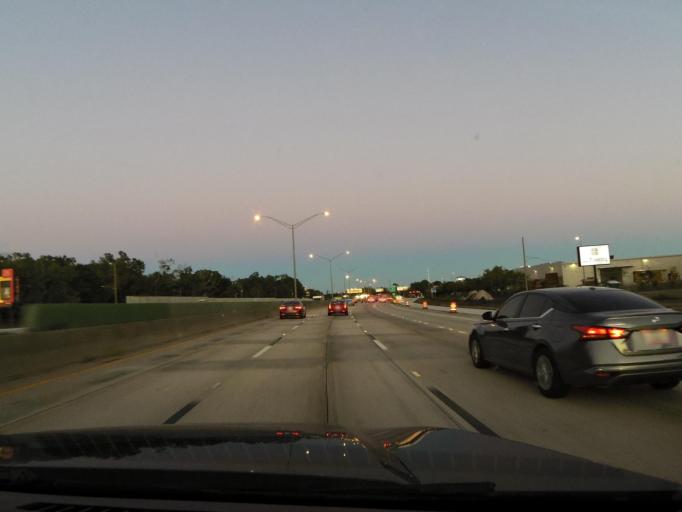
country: US
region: Florida
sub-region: Duval County
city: Jacksonville
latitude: 30.3174
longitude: -81.7361
